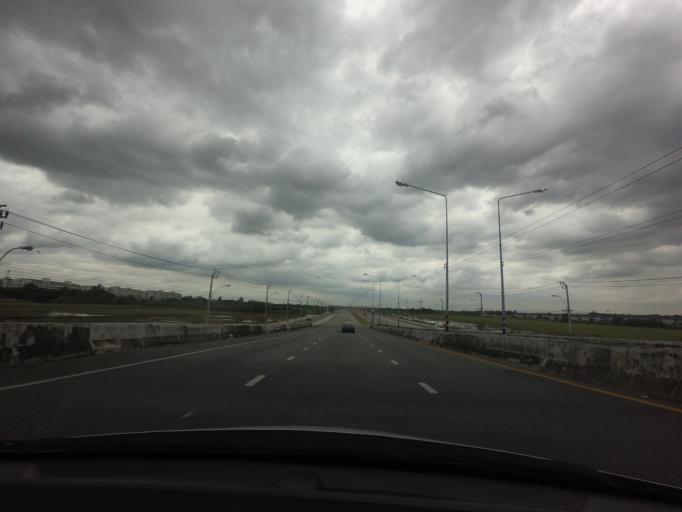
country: TH
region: Bangkok
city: Saphan Sung
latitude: 13.7549
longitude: 100.7263
